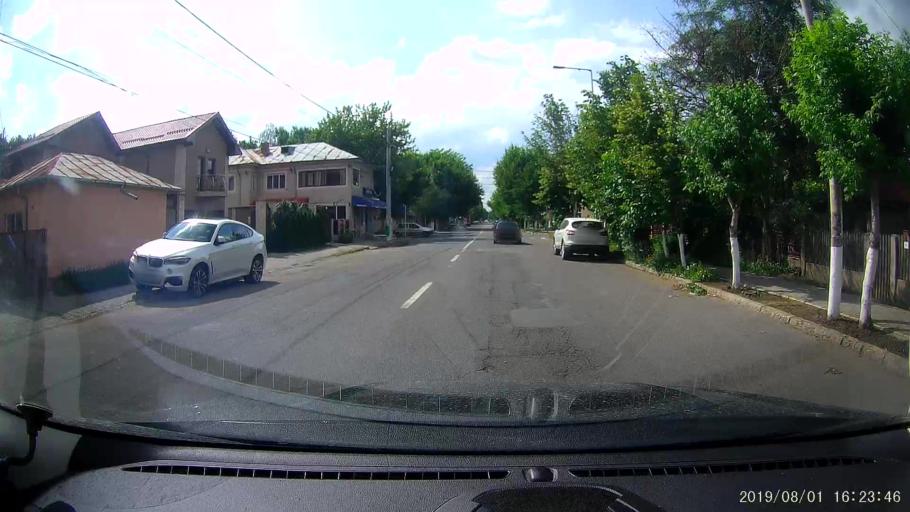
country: RO
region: Calarasi
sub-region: Municipiul Calarasi
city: Calarasi
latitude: 44.1962
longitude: 27.3337
